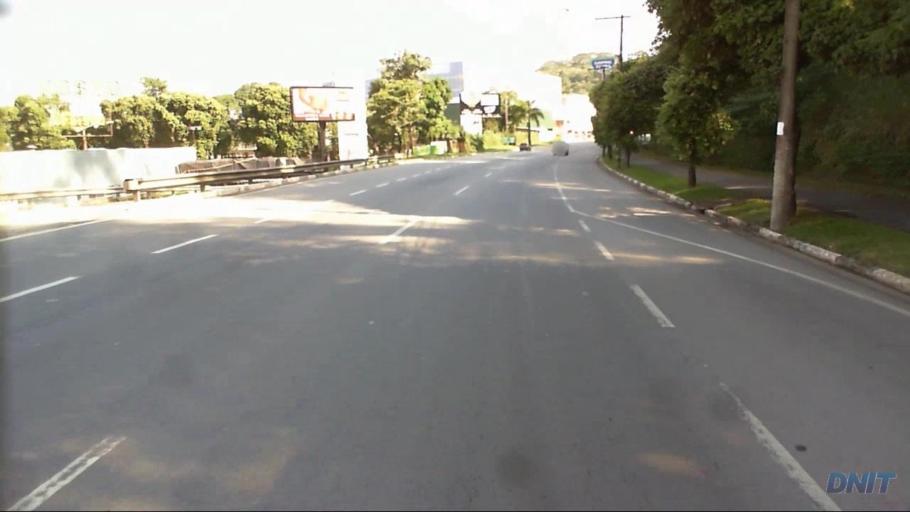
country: BR
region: Minas Gerais
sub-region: Ipatinga
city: Ipatinga
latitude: -19.4933
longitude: -42.5645
